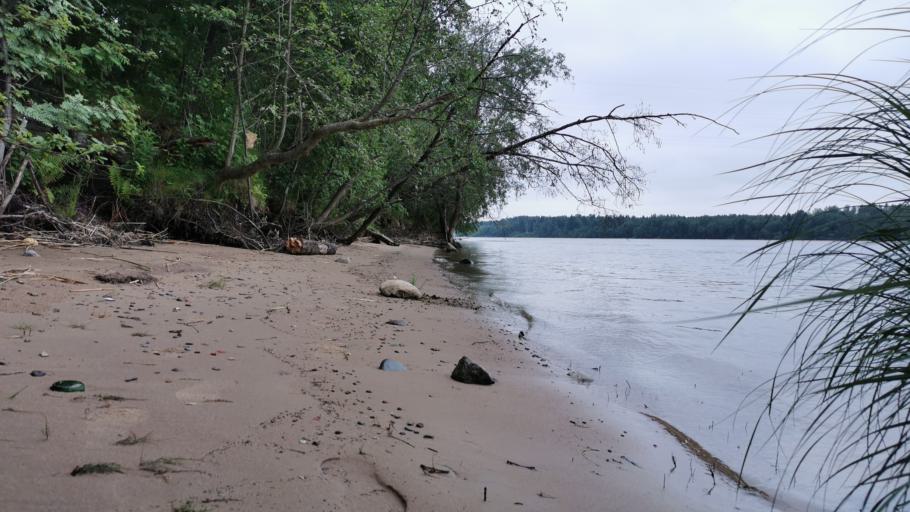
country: RU
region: Leningrad
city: Kirovsk
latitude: 59.9195
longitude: 30.9893
